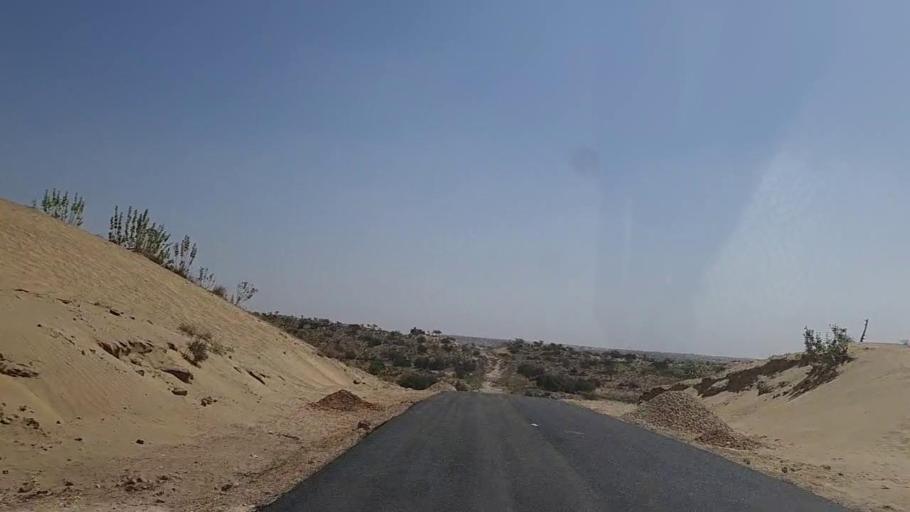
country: PK
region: Sindh
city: Diplo
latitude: 24.4785
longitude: 69.5300
